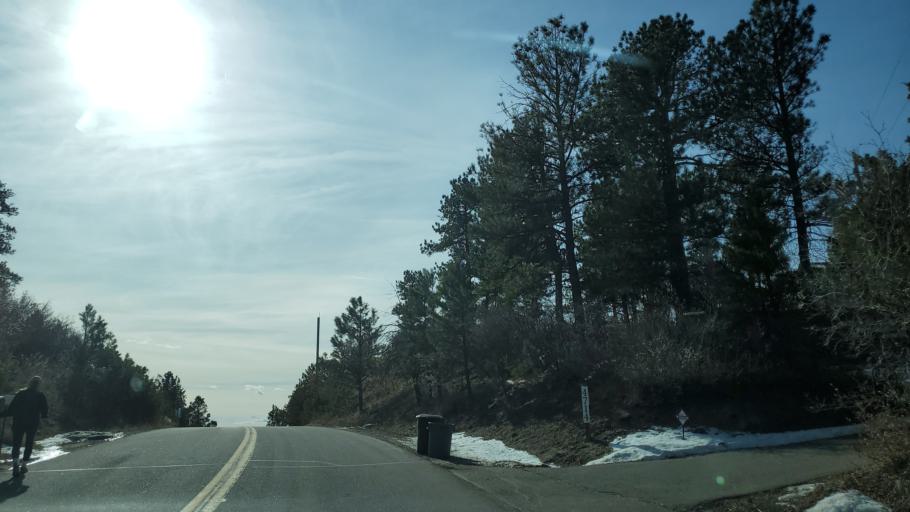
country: US
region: Colorado
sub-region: Douglas County
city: Castle Pines
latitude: 39.4313
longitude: -104.8759
